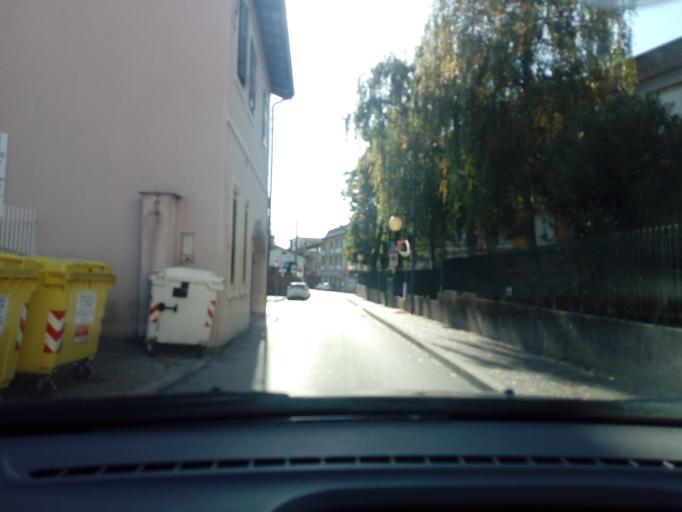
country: IT
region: Friuli Venezia Giulia
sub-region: Provincia di Gorizia
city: Cormons
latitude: 45.9594
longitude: 13.4718
